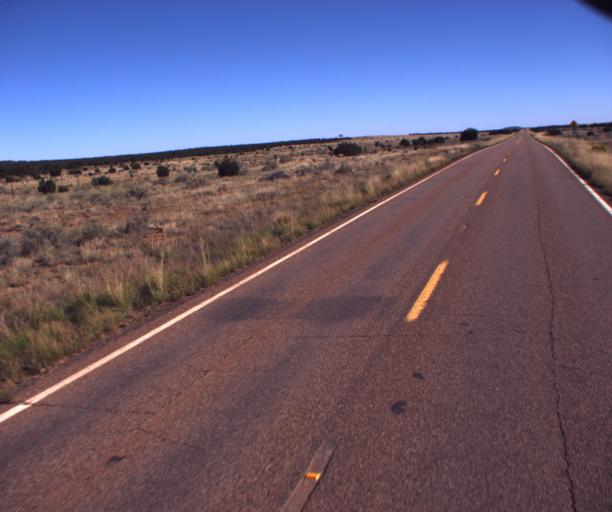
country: US
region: Arizona
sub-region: Navajo County
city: Heber-Overgaard
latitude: 34.4726
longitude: -110.3578
